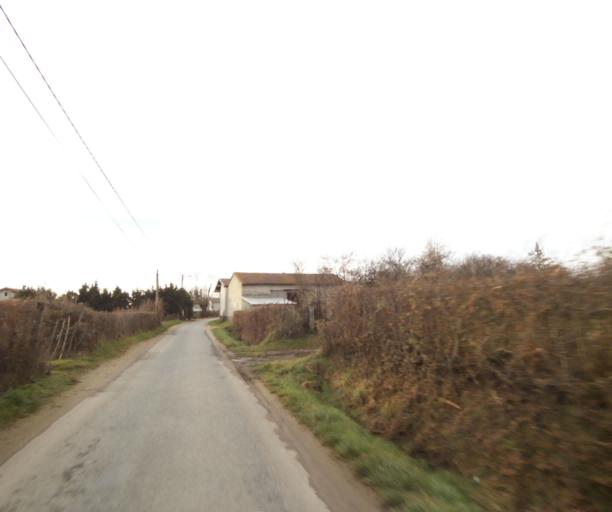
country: FR
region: Rhone-Alpes
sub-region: Departement de la Loire
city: Sury-le-Comtal
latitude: 45.5301
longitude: 4.1663
